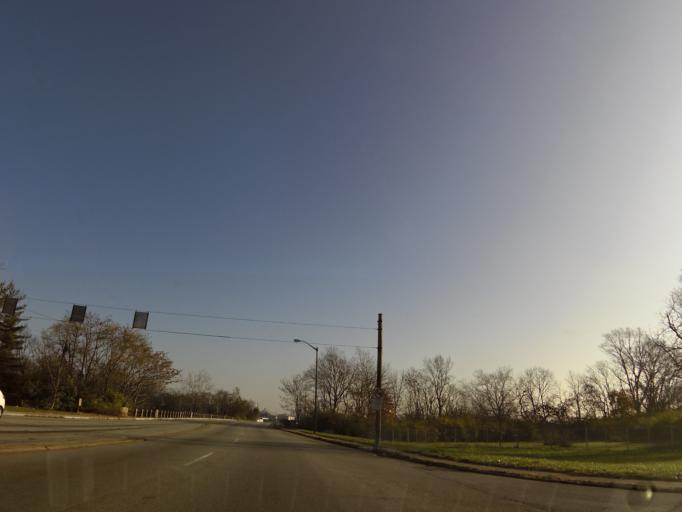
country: US
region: Indiana
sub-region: Marion County
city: Indianapolis
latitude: 39.7881
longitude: -86.1997
